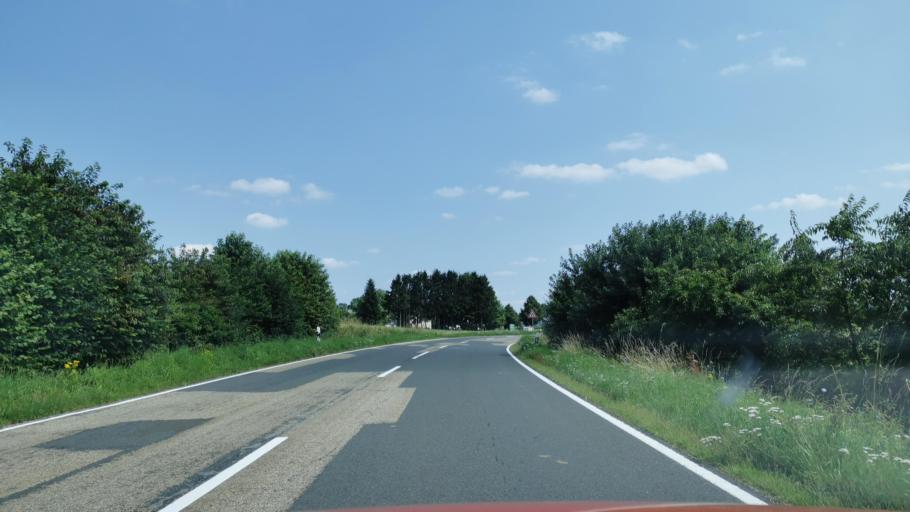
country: DE
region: Rheinland-Pfalz
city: Talling
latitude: 49.7621
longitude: 6.9460
